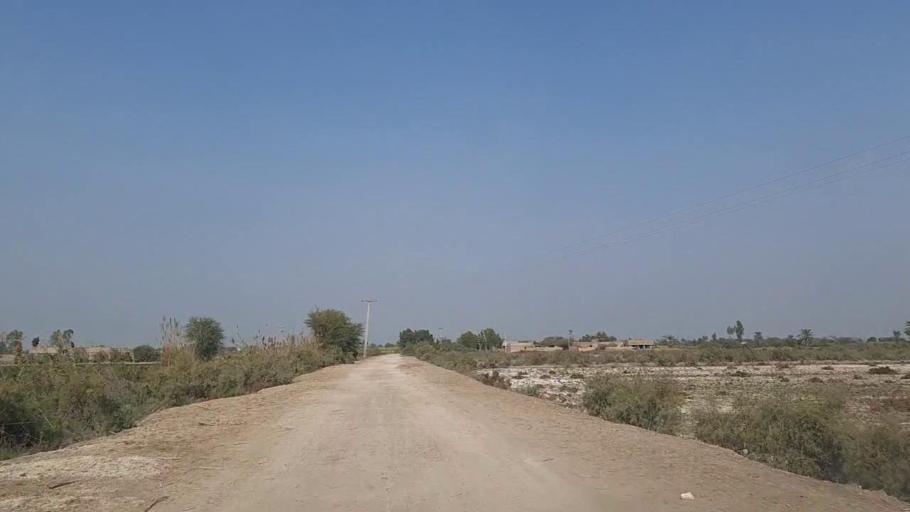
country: PK
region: Sindh
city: Daur
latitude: 26.4863
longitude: 68.4514
